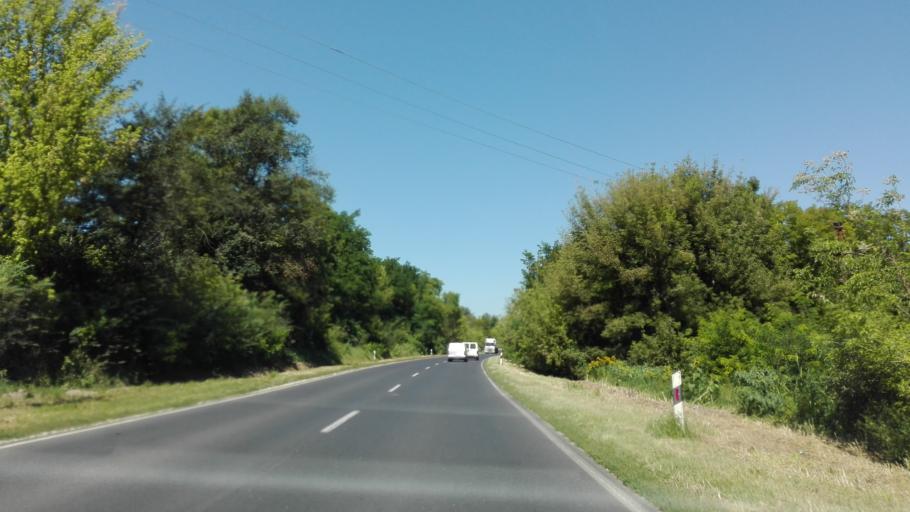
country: HU
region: Fejer
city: Mezoszilas
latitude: 46.7927
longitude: 18.4964
